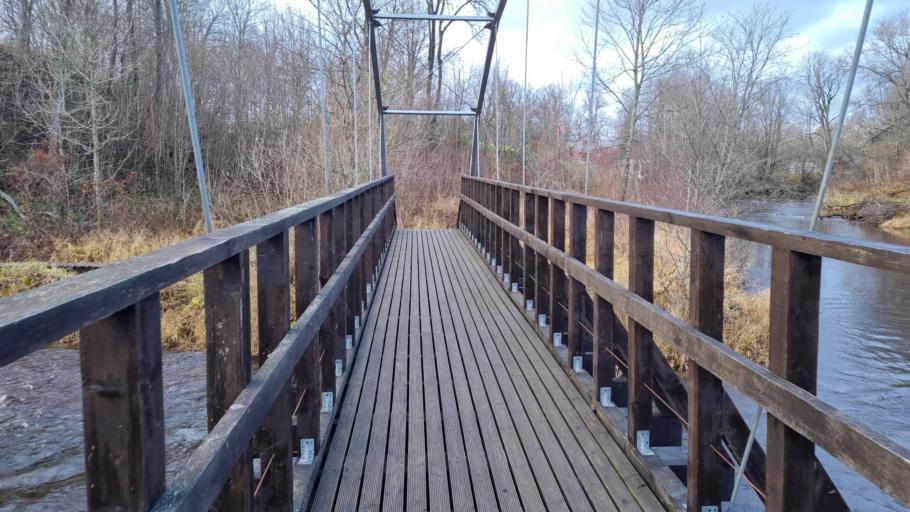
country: LV
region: Malpils
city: Malpils
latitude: 57.0045
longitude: 24.9646
